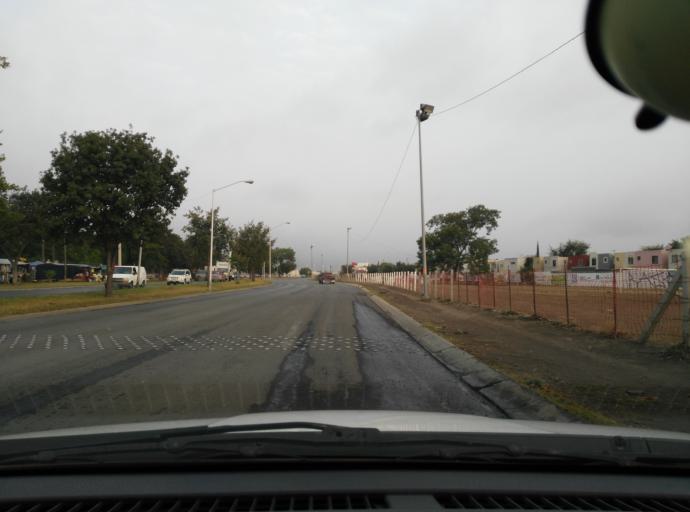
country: MX
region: Nuevo Leon
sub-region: Apodaca
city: Fraccionamiento Cosmopolis Octavo Sector
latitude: 25.7717
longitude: -100.2528
